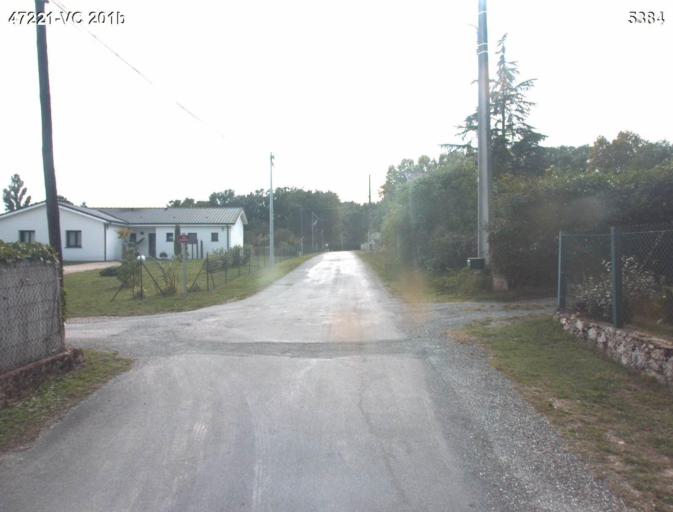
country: FR
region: Aquitaine
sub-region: Departement du Lot-et-Garonne
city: Mezin
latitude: 44.0896
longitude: 0.1901
